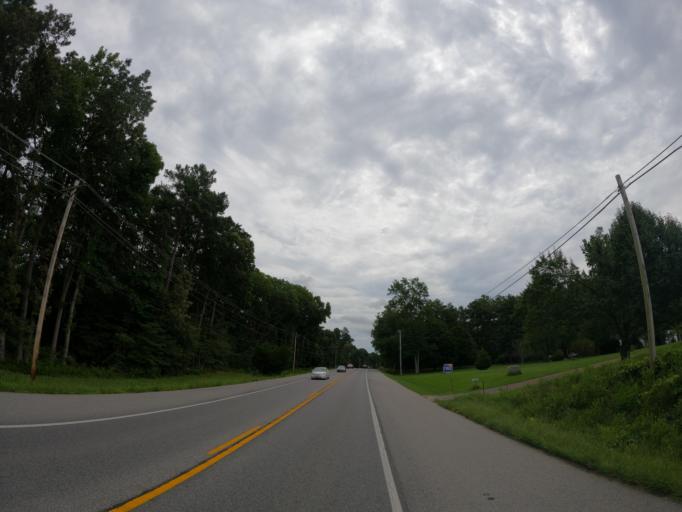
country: US
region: Maryland
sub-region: Saint Mary's County
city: California
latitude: 38.2387
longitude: -76.5377
